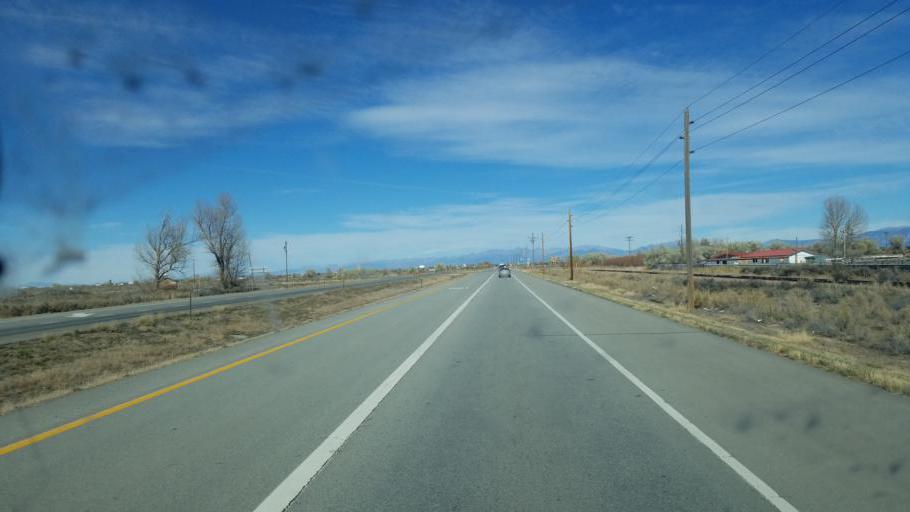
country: US
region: Colorado
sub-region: Alamosa County
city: Alamosa
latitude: 37.4278
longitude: -105.8917
